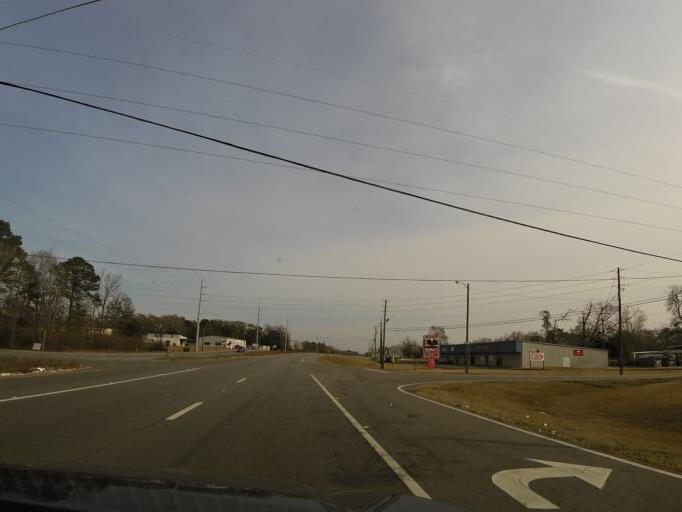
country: US
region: Alabama
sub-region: Houston County
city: Cowarts
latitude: 31.1924
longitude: -85.3040
